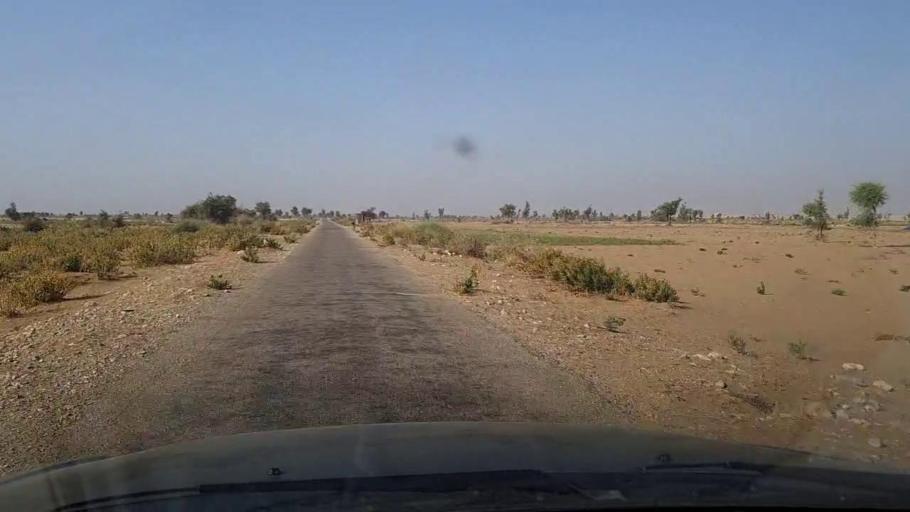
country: PK
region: Sindh
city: Sann
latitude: 25.9677
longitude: 68.0511
